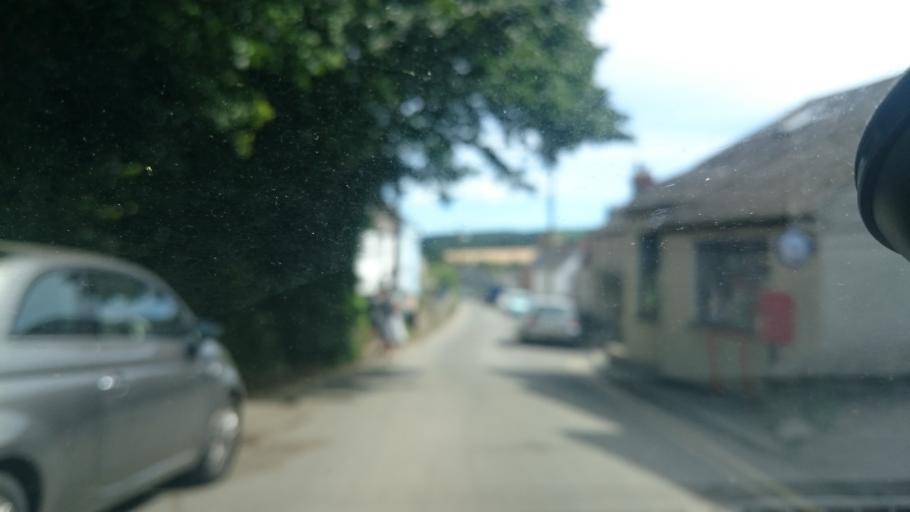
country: GB
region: Wales
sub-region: Pembrokeshire
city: Llangwm
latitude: 51.7491
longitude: -4.9145
